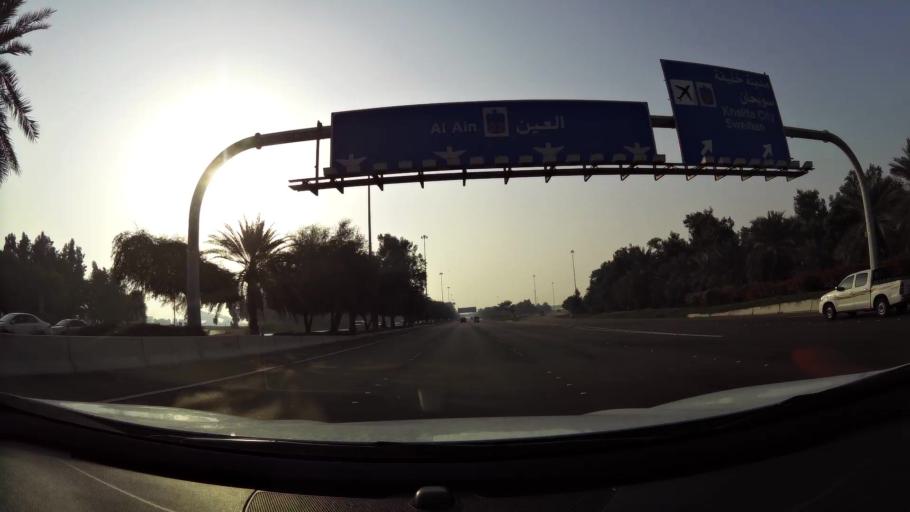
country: AE
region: Abu Dhabi
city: Abu Dhabi
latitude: 24.3981
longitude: 54.5317
